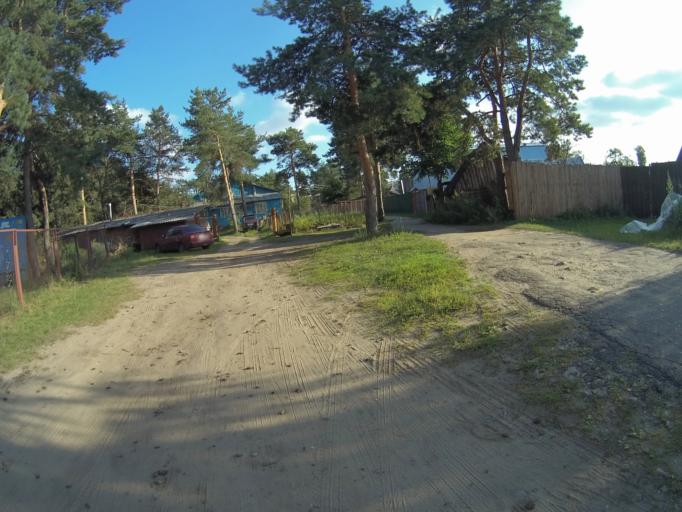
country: RU
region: Vladimir
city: Kommunar
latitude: 56.1225
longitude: 40.4610
